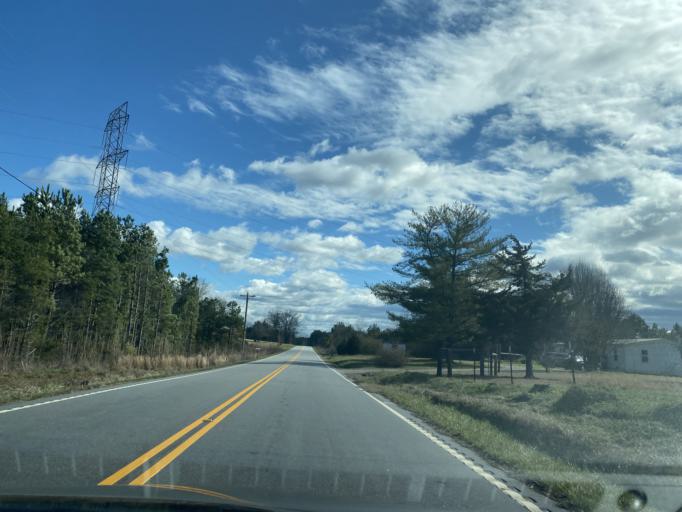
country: US
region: South Carolina
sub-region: Spartanburg County
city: Cowpens
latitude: 35.0980
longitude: -81.7555
